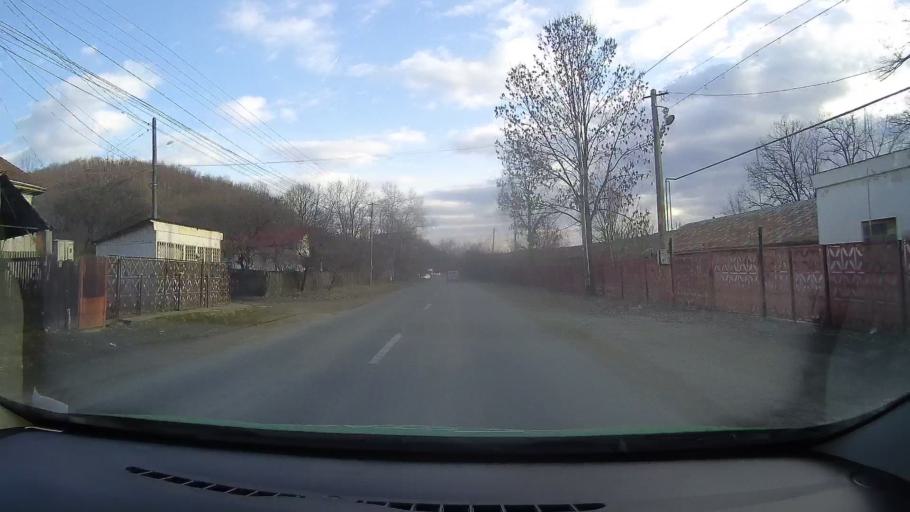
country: RO
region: Dambovita
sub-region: Comuna Ocnita
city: Ocnita
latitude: 44.9607
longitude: 25.5497
